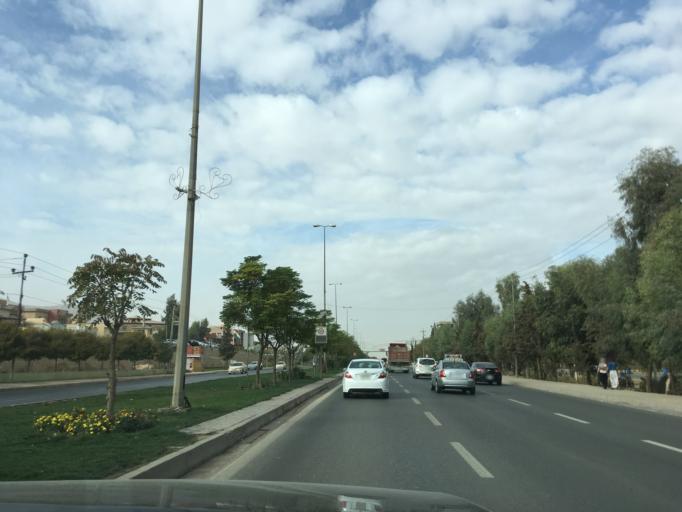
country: IQ
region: Dahuk
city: Dihok
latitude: 36.8472
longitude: 43.0210
